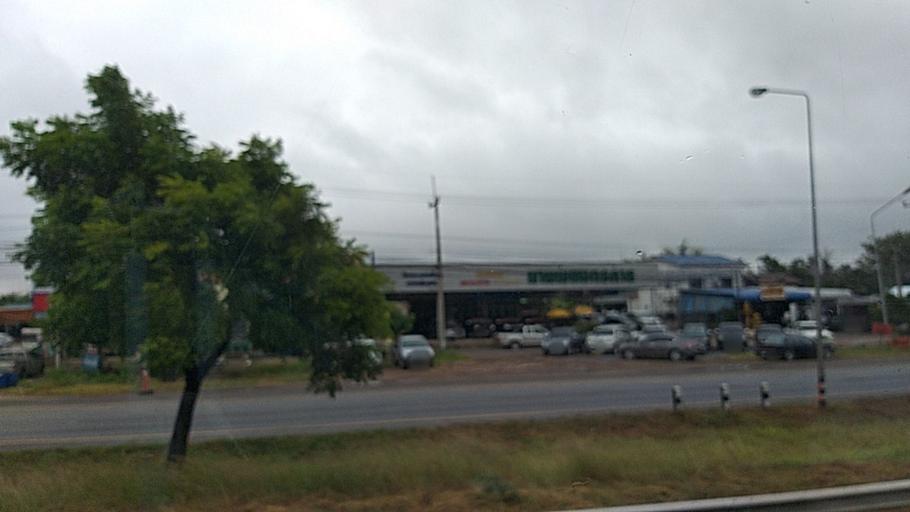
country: TH
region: Nakhon Ratchasima
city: Non Sung
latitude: 15.1066
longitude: 102.2915
